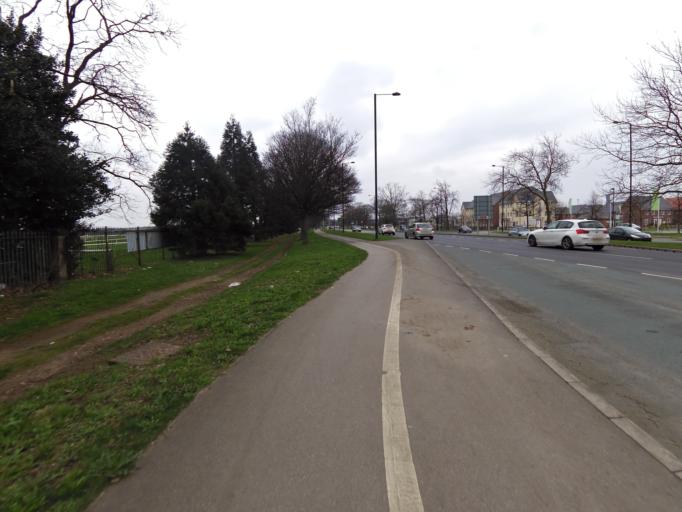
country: GB
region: England
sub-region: Doncaster
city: Doncaster
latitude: 53.5186
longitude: -1.1060
